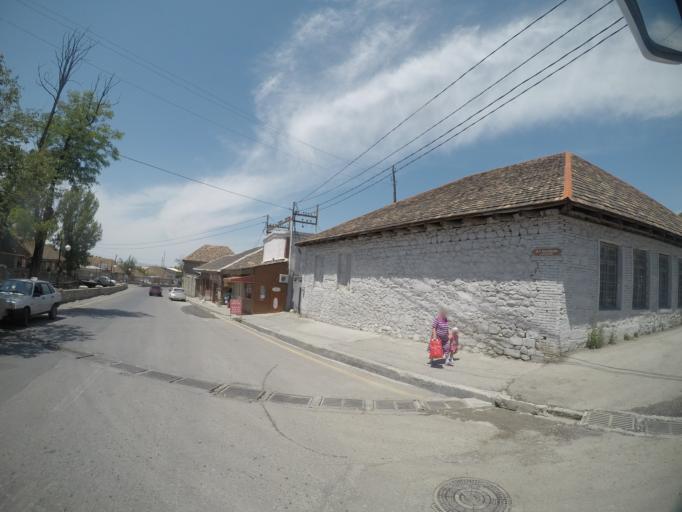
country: AZ
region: Shaki City
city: Sheki
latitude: 41.2013
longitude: 47.1844
